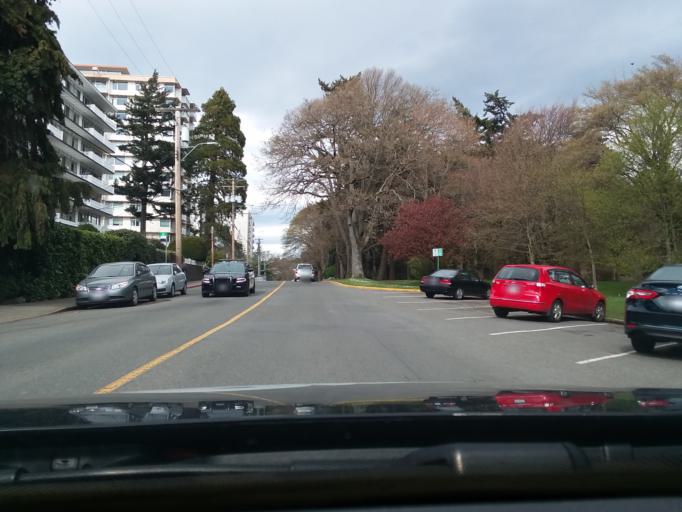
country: CA
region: British Columbia
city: Victoria
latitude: 48.4132
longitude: -123.3674
